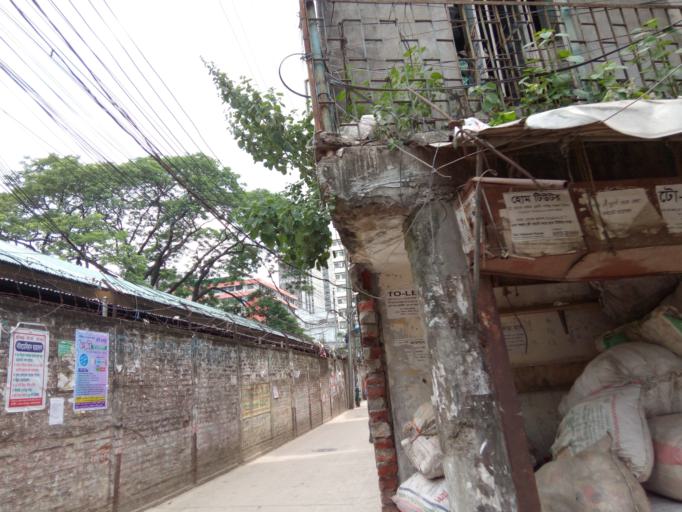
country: BD
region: Dhaka
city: Paltan
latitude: 23.7291
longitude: 90.4205
